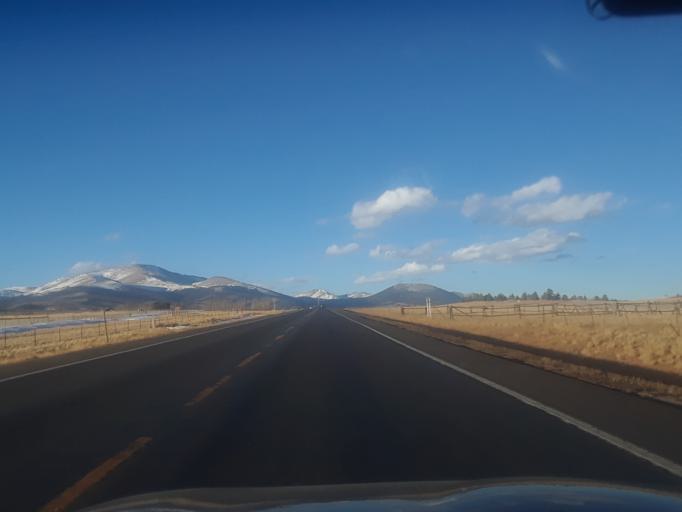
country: US
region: Colorado
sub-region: Park County
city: Fairplay
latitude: 39.1913
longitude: -105.9971
